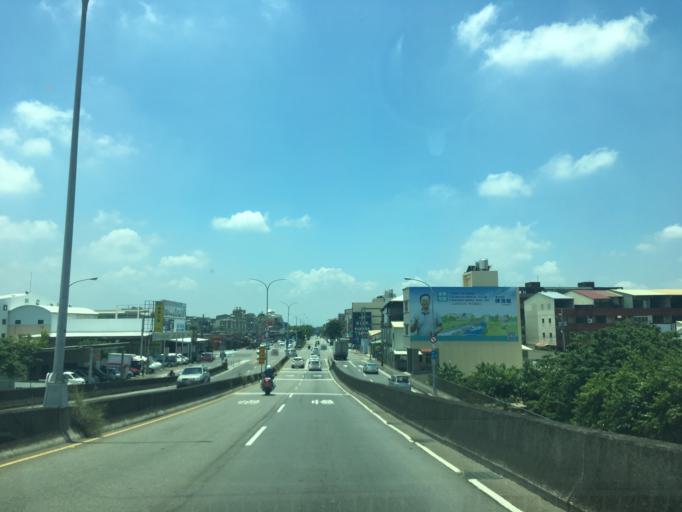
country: TW
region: Taiwan
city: Fengyuan
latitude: 24.2481
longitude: 120.7032
